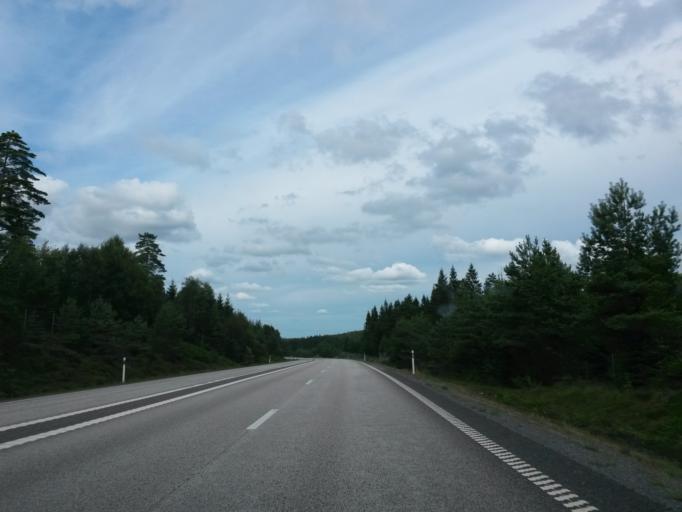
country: SE
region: Vaestra Goetaland
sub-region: Marks Kommun
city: Fritsla
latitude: 57.5430
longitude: 12.8139
